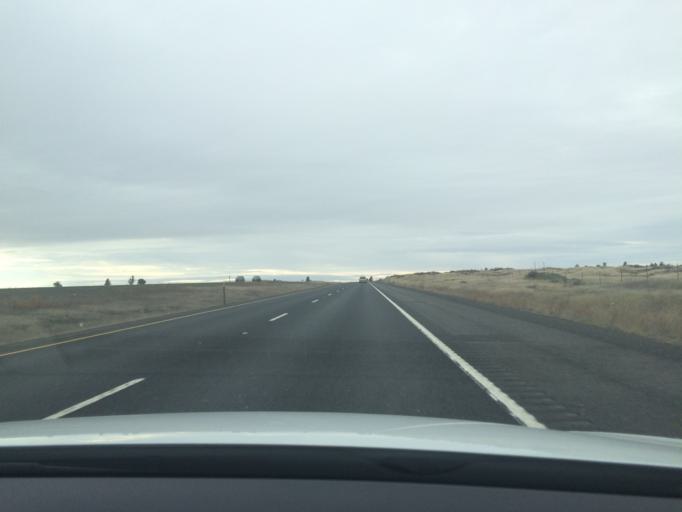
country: US
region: Washington
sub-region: Spokane County
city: Medical Lake
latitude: 47.3887
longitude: -117.8528
